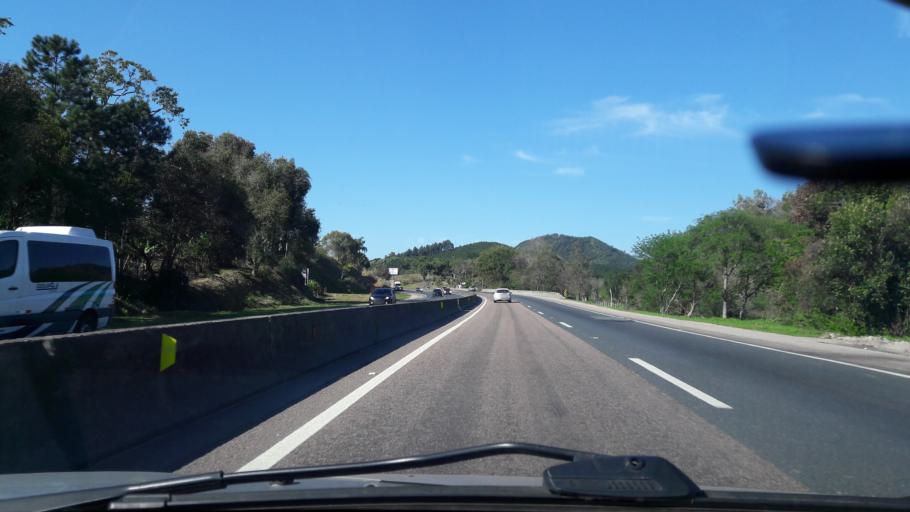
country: BR
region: Santa Catarina
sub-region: Tijucas
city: Tijucas
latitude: -27.3084
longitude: -48.6329
